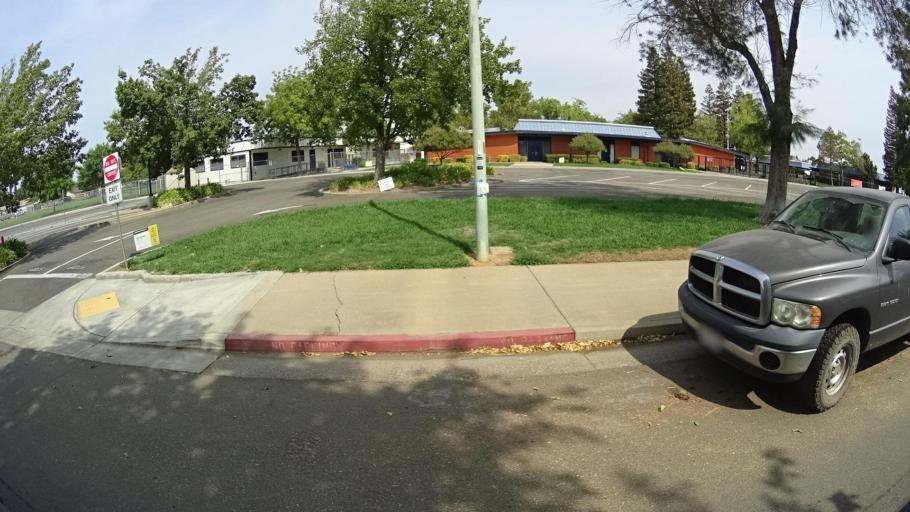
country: US
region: California
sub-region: Sacramento County
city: Elk Grove
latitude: 38.4196
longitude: -121.3776
